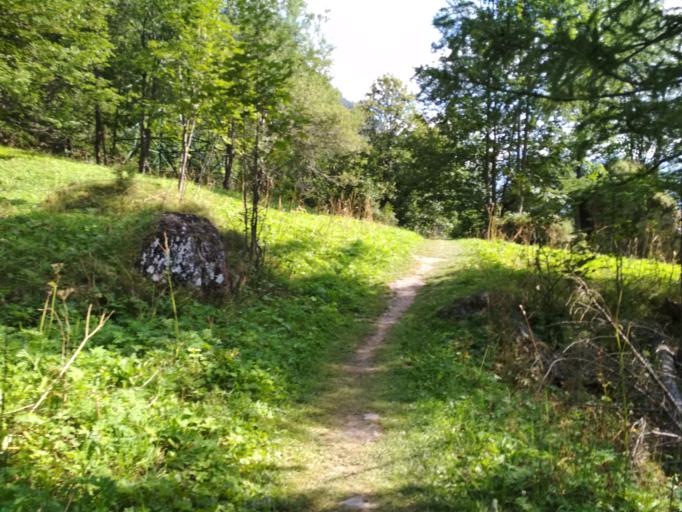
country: IT
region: Aosta Valley
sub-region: Valle d'Aosta
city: Gressoney-La-Trinite
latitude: 45.8066
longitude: 7.8270
